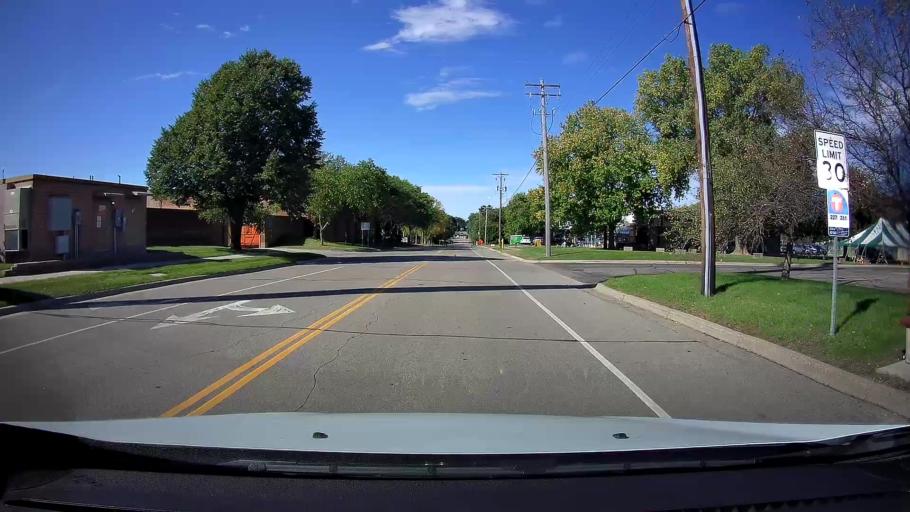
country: US
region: Minnesota
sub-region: Ramsey County
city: Roseville
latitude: 45.0228
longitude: -93.1474
